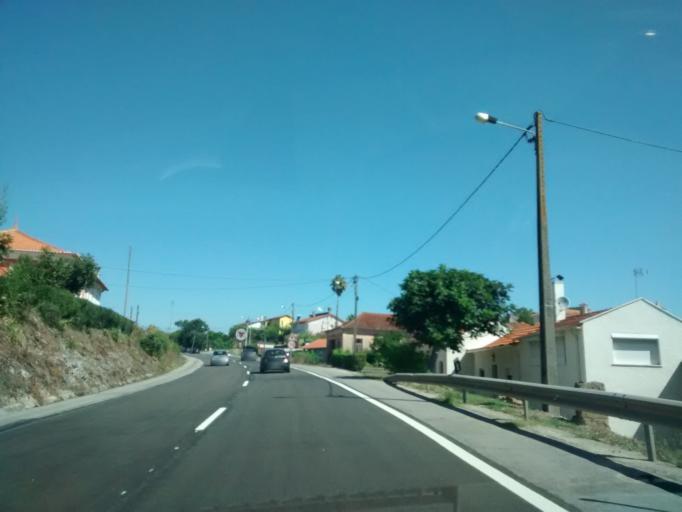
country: PT
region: Aveiro
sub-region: Oliveira do Bairro
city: Oliveira do Bairro
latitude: 40.5313
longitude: -8.5085
